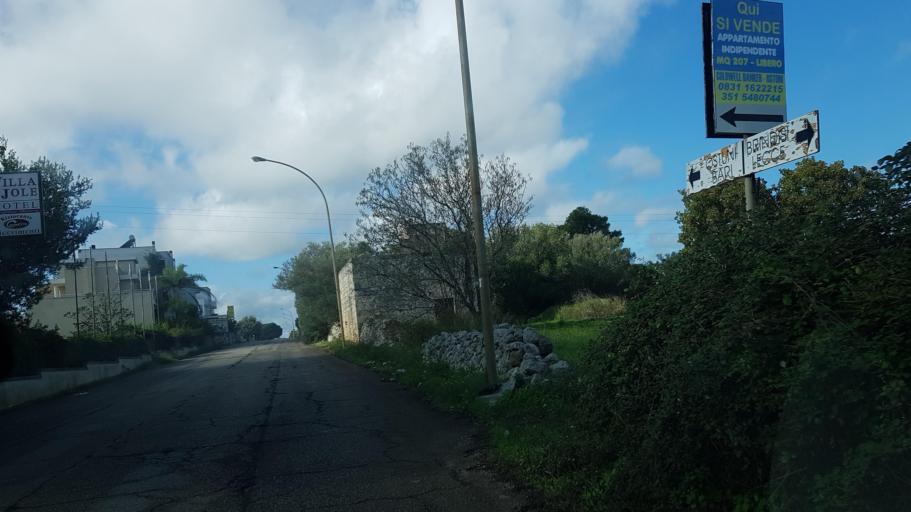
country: IT
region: Apulia
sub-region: Provincia di Brindisi
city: Carovigno
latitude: 40.7061
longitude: 17.6500
